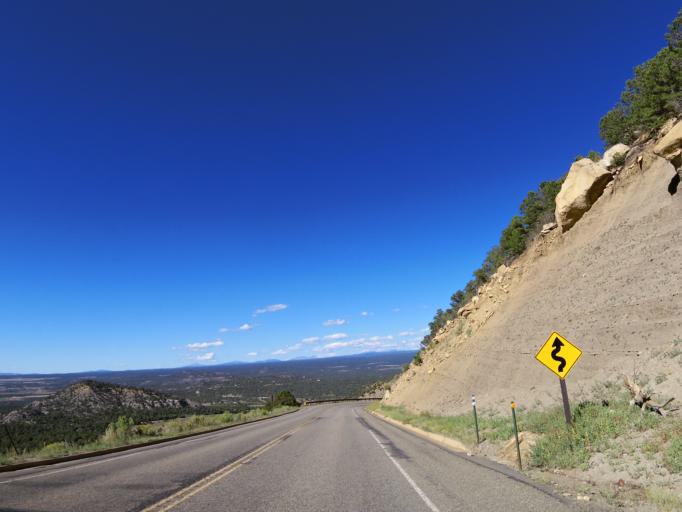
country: US
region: Colorado
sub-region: Montezuma County
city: Mancos
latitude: 37.3212
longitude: -108.4171
